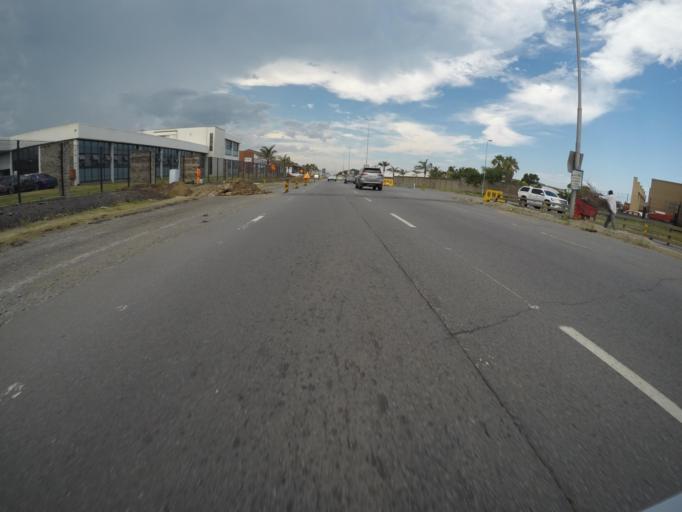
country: ZA
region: Eastern Cape
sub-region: Buffalo City Metropolitan Municipality
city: East London
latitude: -33.0298
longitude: 27.8868
